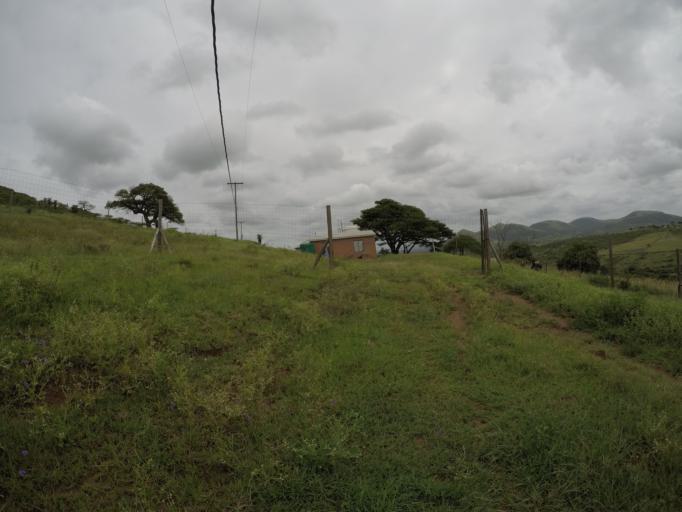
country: ZA
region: KwaZulu-Natal
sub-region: uThungulu District Municipality
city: Empangeni
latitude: -28.6174
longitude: 31.8910
